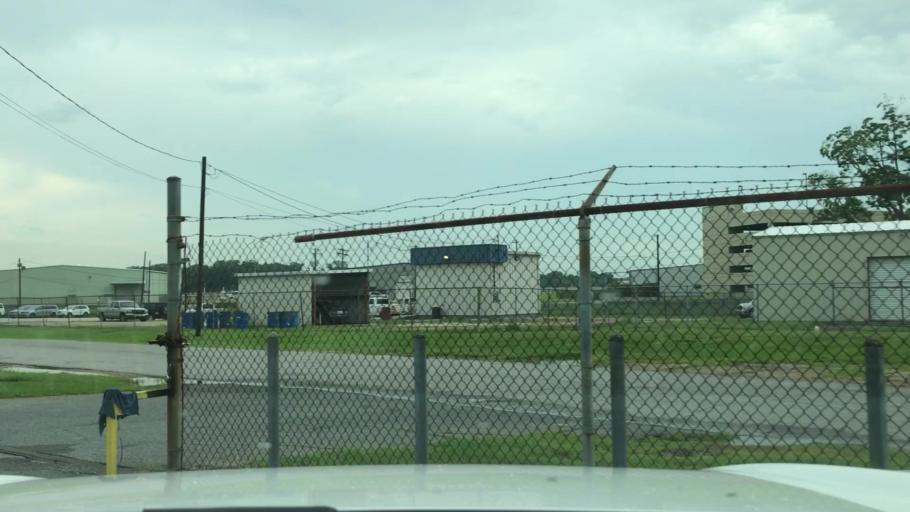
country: US
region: Louisiana
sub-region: East Baton Rouge Parish
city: Brownsfield
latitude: 30.5341
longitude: -91.1599
